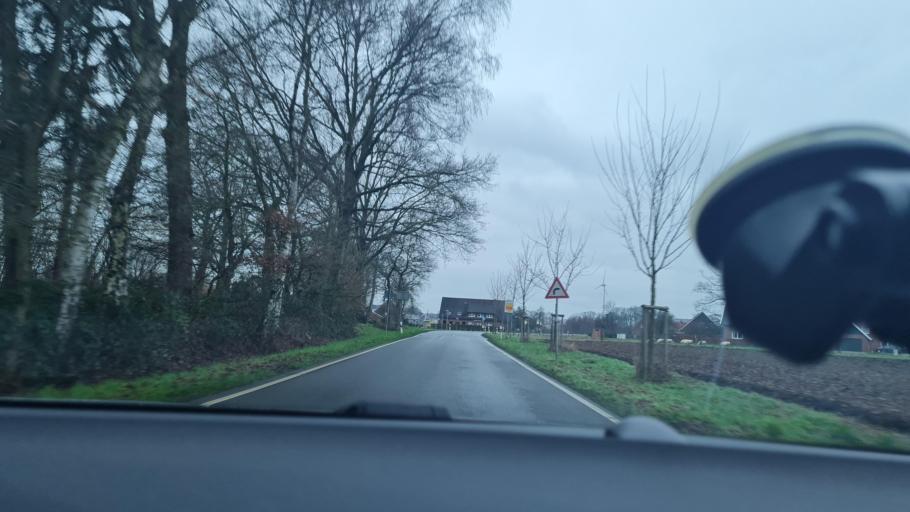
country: DE
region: North Rhine-Westphalia
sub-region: Regierungsbezirk Munster
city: Heiden
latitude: 51.7779
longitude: 6.9173
